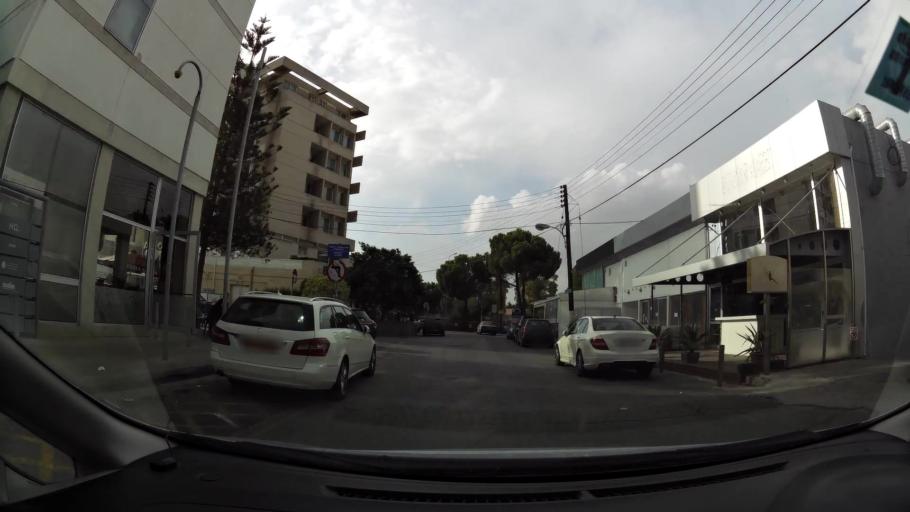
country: CY
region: Lefkosia
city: Nicosia
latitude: 35.1610
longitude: 33.3441
